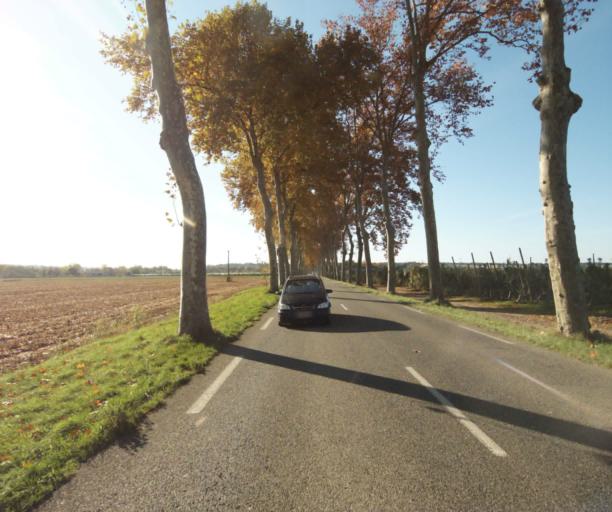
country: FR
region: Midi-Pyrenees
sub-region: Departement du Tarn-et-Garonne
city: Montech
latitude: 43.9540
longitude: 1.1979
